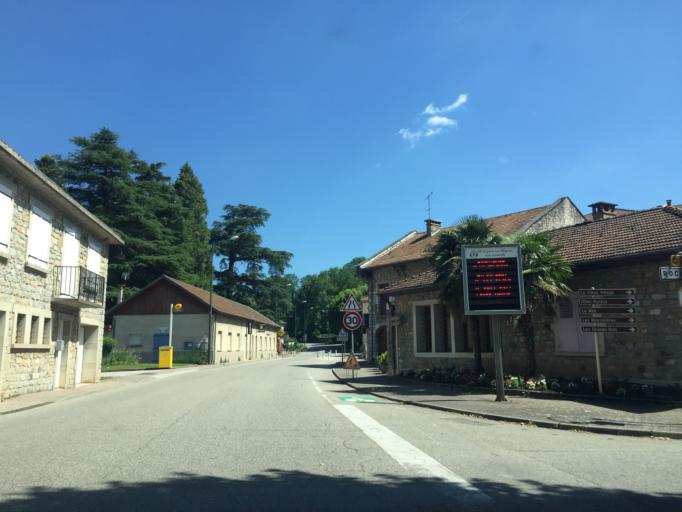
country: FR
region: Rhone-Alpes
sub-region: Departement de l'Isere
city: Saint-Hilaire-du-Rosier
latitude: 45.0598
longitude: 5.2494
